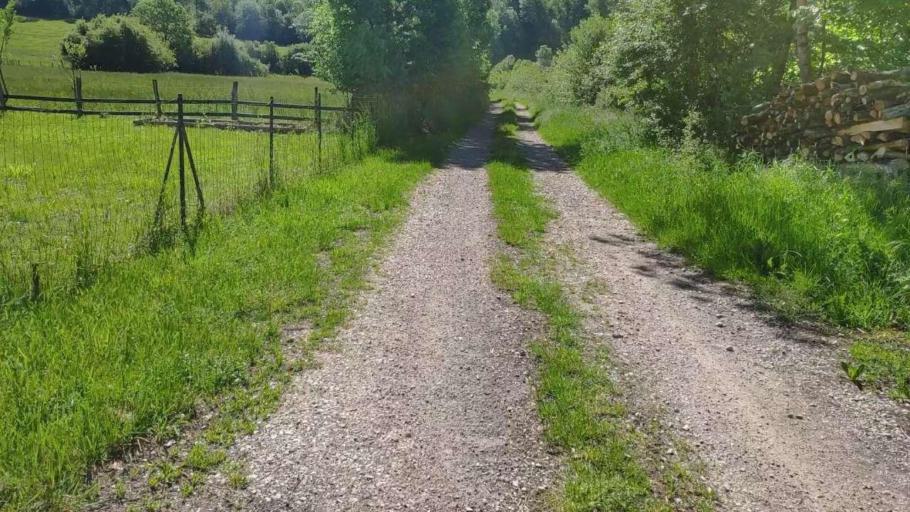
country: FR
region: Franche-Comte
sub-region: Departement du Jura
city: Poligny
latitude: 46.7269
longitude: 5.7492
